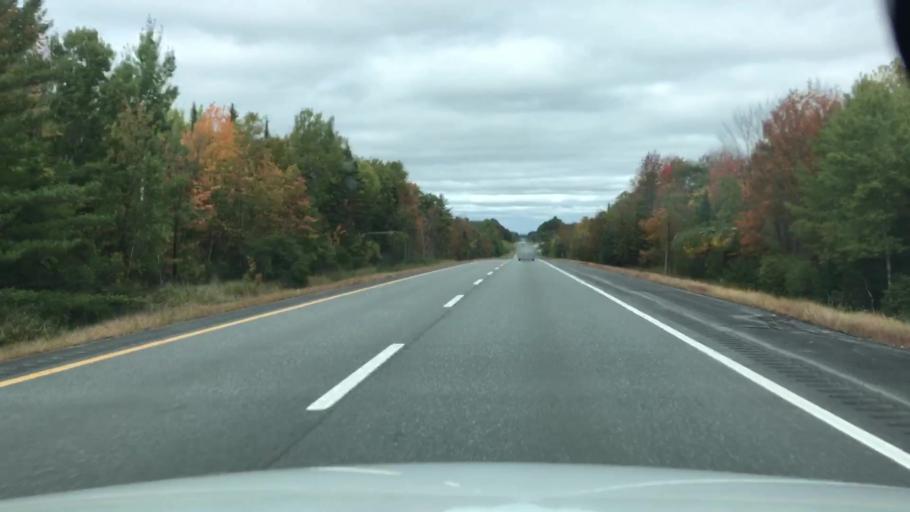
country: US
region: Maine
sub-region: Waldo County
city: Burnham
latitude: 44.7375
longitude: -69.4310
